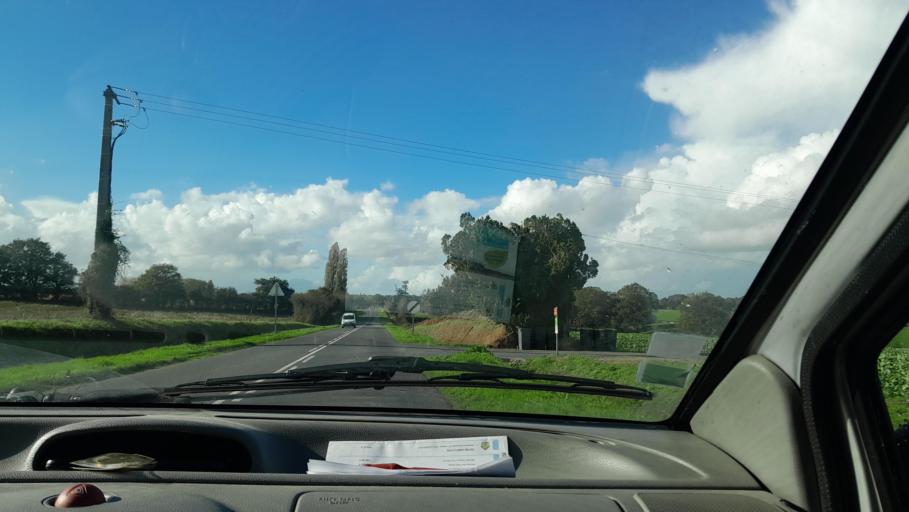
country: FR
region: Pays de la Loire
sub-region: Departement de la Mayenne
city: Cosse-le-Vivien
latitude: 47.9529
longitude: -0.9307
